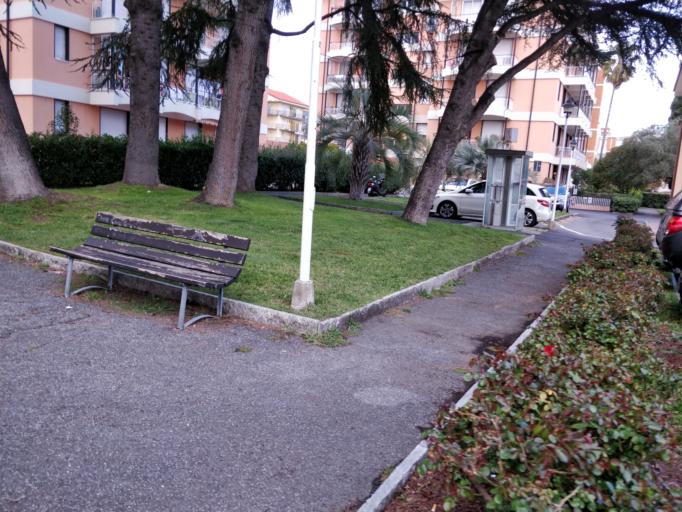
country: IT
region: Liguria
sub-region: Provincia di Imperia
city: San Bartolomeo al Mare
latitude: 43.9213
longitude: 8.1007
